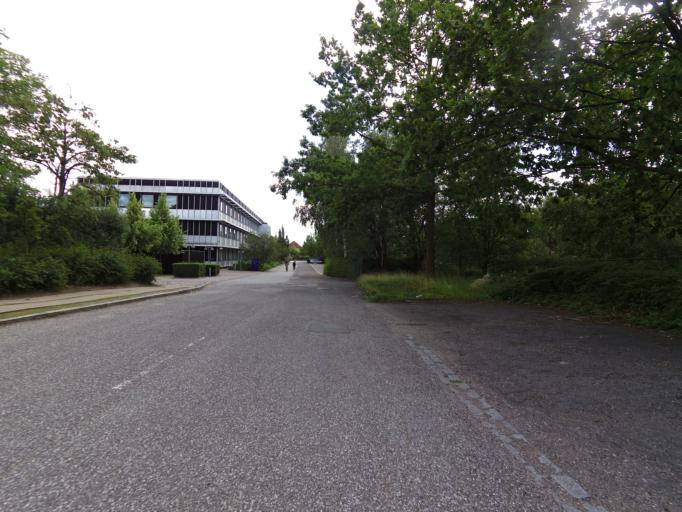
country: DK
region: Capital Region
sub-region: Frederiksberg Kommune
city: Frederiksberg
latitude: 55.7215
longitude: 12.5409
